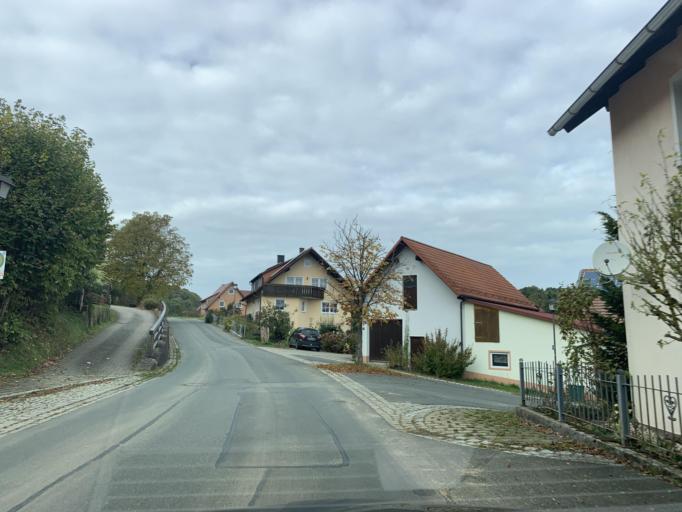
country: DE
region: Bavaria
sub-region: Upper Franconia
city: Gossweinstein
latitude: 49.7882
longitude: 11.3100
